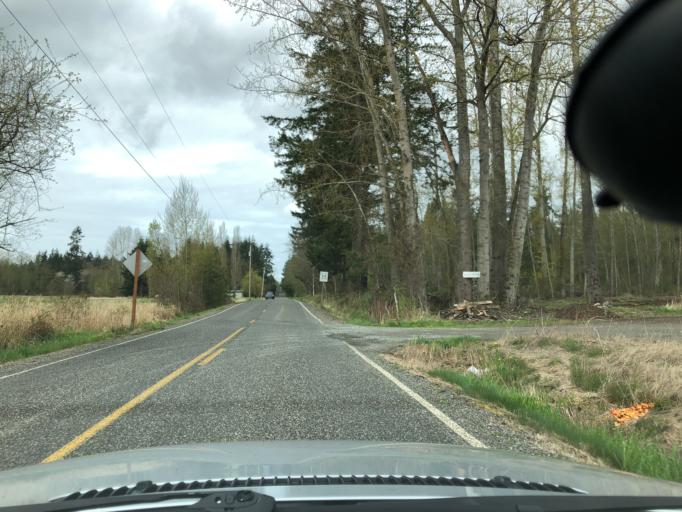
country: US
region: Washington
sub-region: Whatcom County
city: Birch Bay
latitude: 48.9431
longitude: -122.7274
